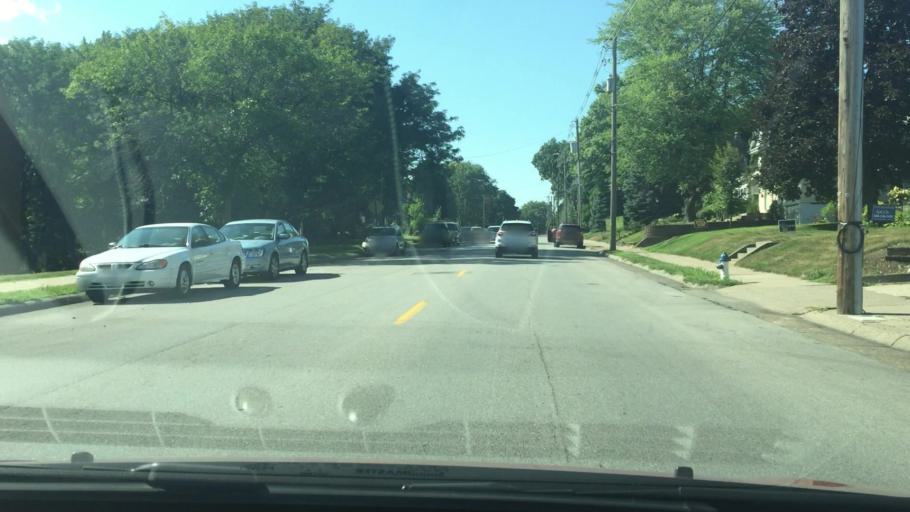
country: US
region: Iowa
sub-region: Muscatine County
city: Muscatine
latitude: 41.4360
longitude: -91.0547
